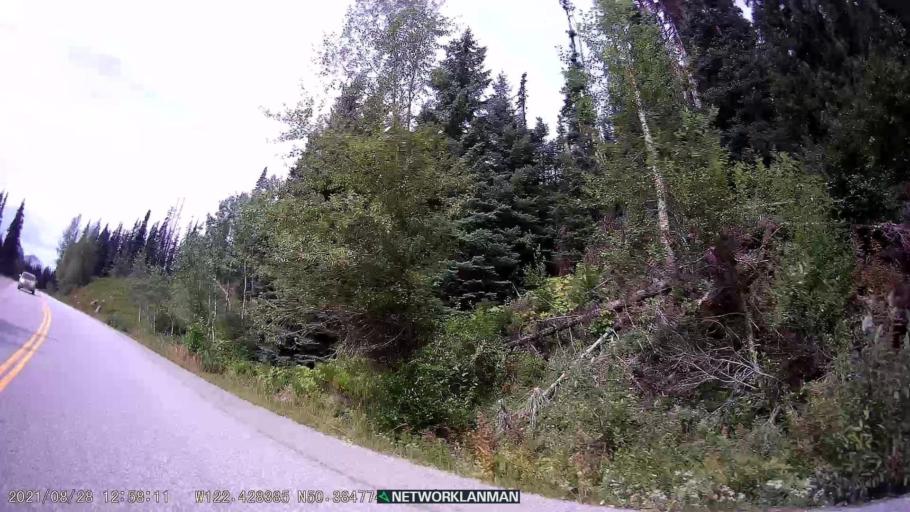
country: CA
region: British Columbia
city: Pemberton
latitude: 50.3848
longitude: -122.4287
